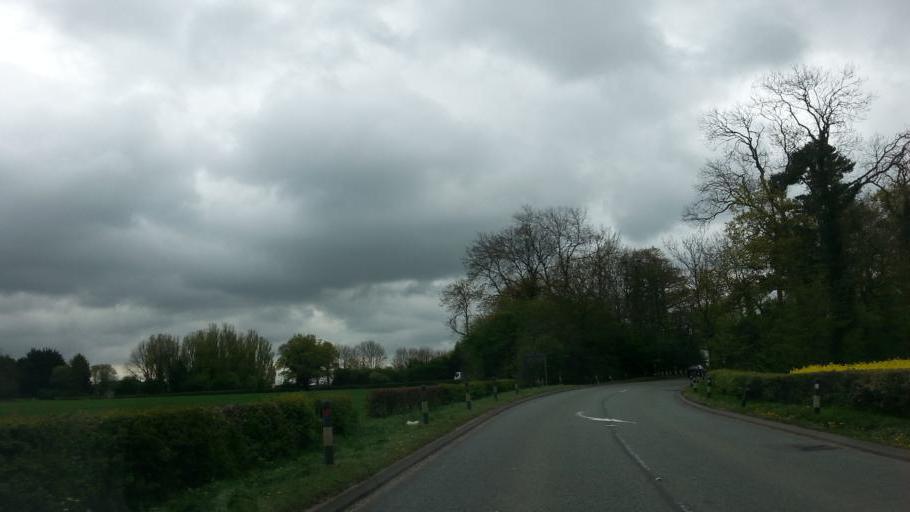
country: GB
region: England
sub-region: Leicestershire
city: Lutterworth
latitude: 52.4239
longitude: -1.2243
